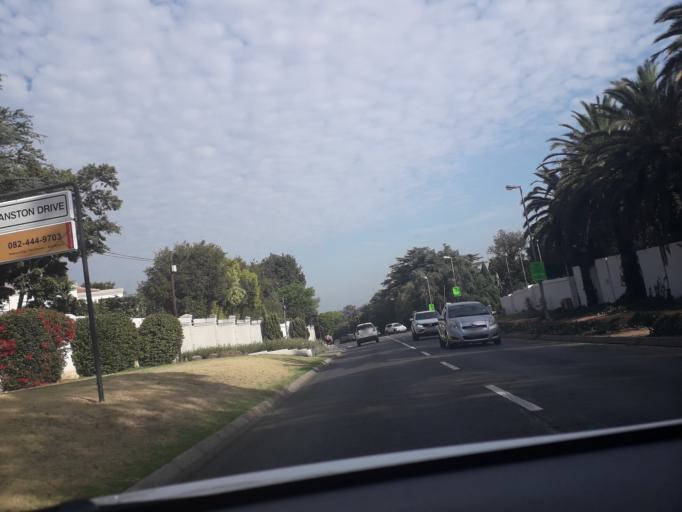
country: ZA
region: Gauteng
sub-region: City of Johannesburg Metropolitan Municipality
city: Johannesburg
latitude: -26.0724
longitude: 28.0058
